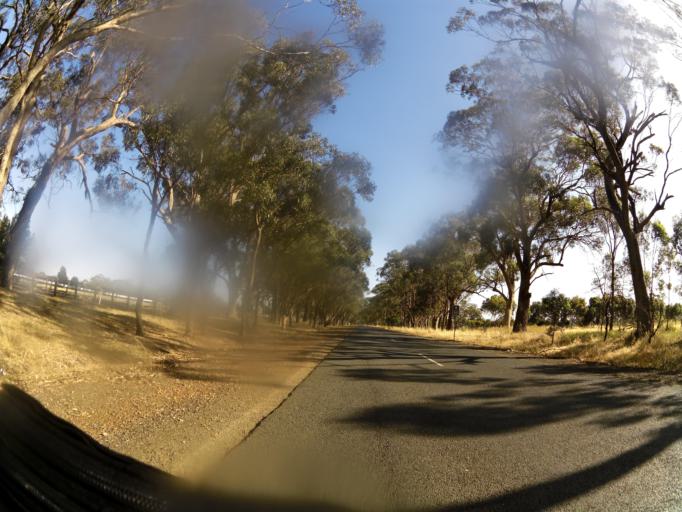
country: AU
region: Victoria
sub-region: Murrindindi
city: Kinglake West
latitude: -36.9708
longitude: 145.1091
